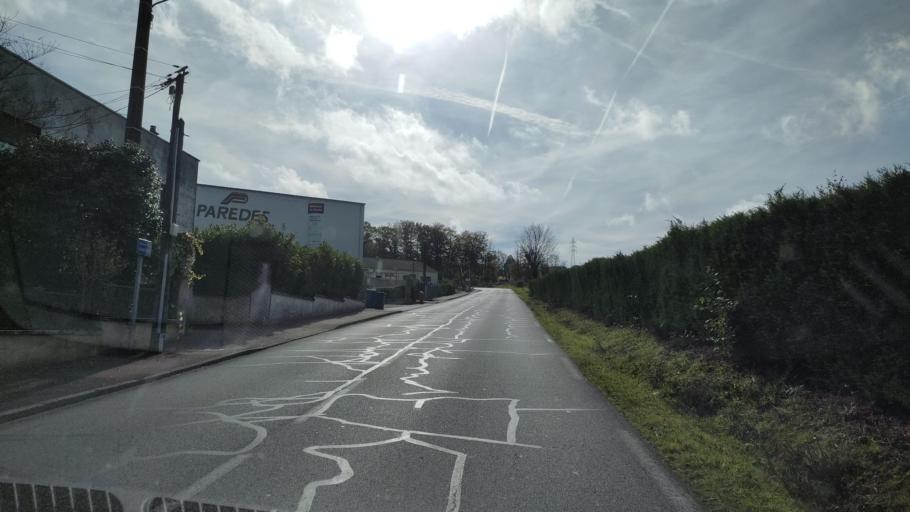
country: FR
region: Limousin
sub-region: Departement de la Haute-Vienne
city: Isle
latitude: 45.8182
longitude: 1.2092
